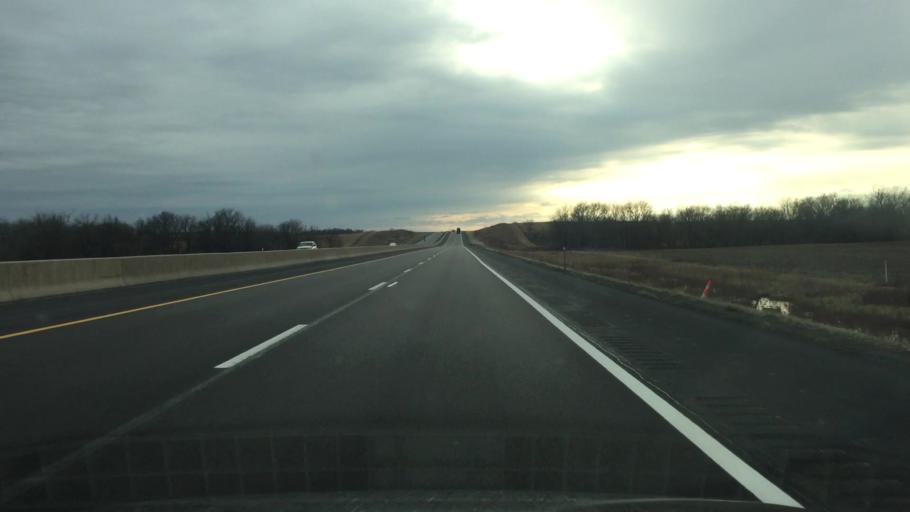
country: US
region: Kansas
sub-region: Lyon County
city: Emporia
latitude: 38.5886
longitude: -96.0811
